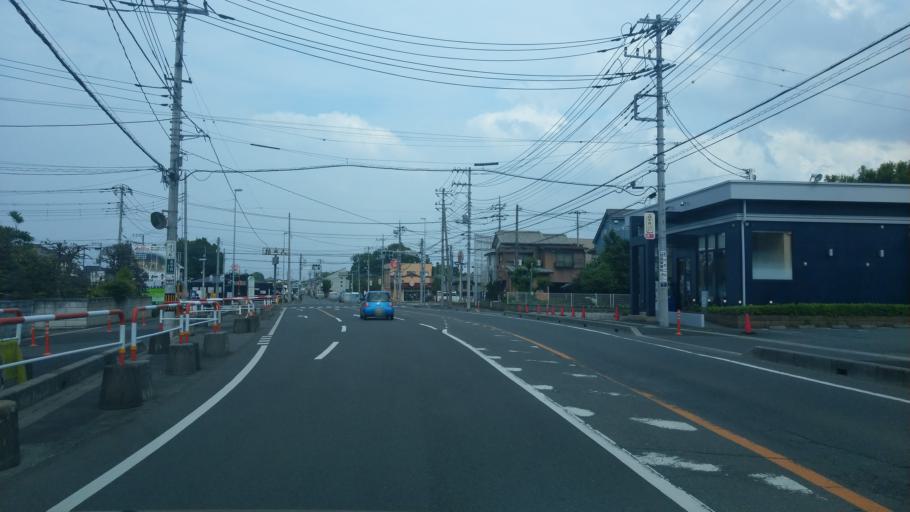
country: JP
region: Saitama
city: Saitama
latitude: 35.9089
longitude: 139.6686
